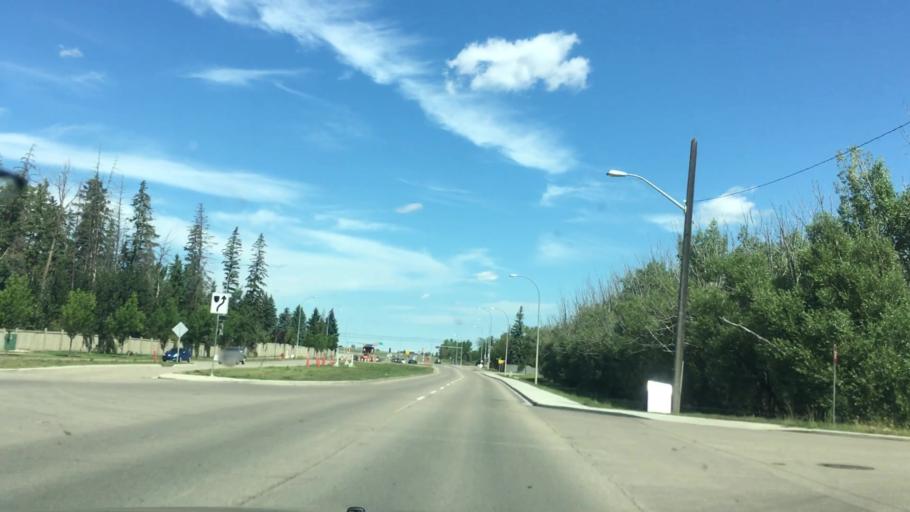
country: CA
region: Alberta
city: Beaumont
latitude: 53.4266
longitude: -113.5164
